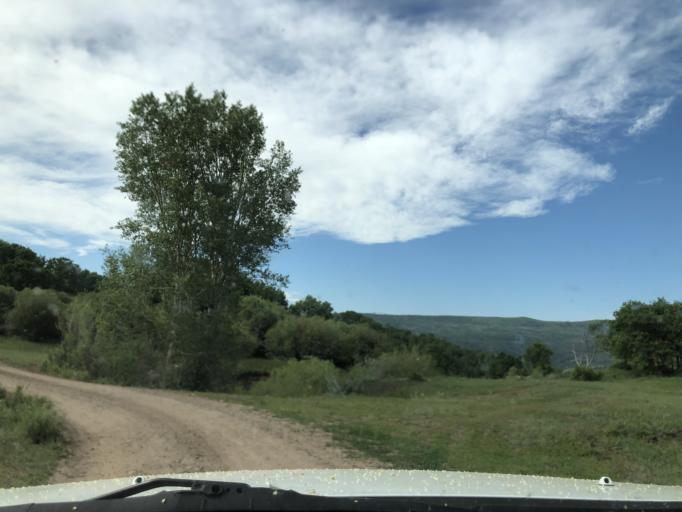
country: US
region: Colorado
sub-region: Delta County
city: Paonia
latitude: 39.0236
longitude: -107.3437
